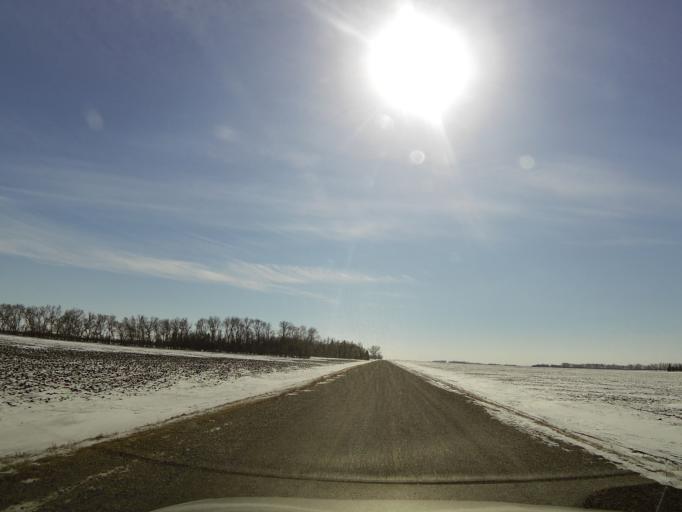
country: US
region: North Dakota
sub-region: Walsh County
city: Grafton
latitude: 48.4103
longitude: -97.2116
